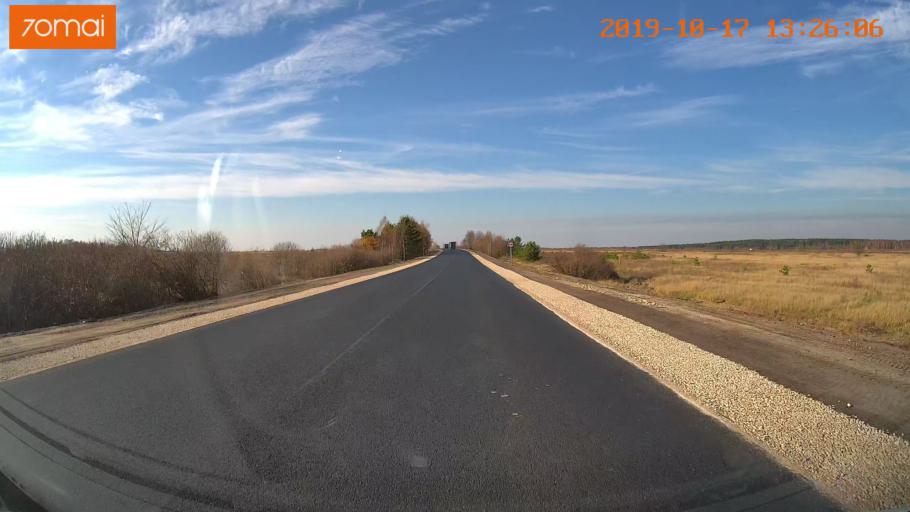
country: RU
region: Rjazan
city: Gus'-Zheleznyy
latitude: 55.1077
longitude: 40.9294
